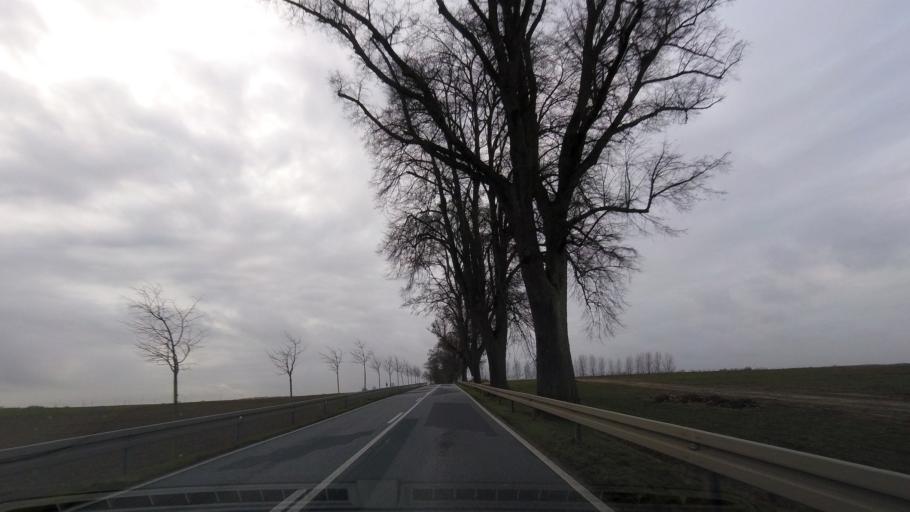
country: DE
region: Mecklenburg-Vorpommern
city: Robel
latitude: 53.3629
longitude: 12.5286
